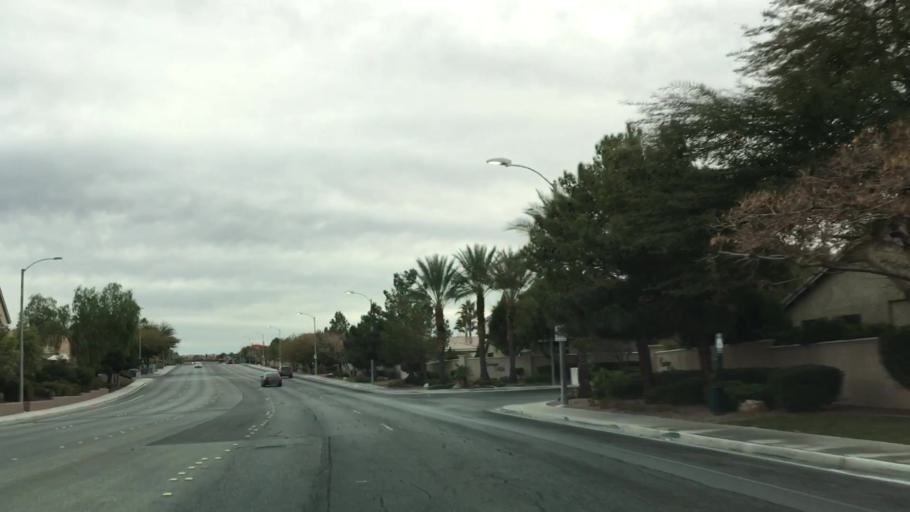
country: US
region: Nevada
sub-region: Clark County
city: Whitney
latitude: 36.0108
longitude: -115.0956
